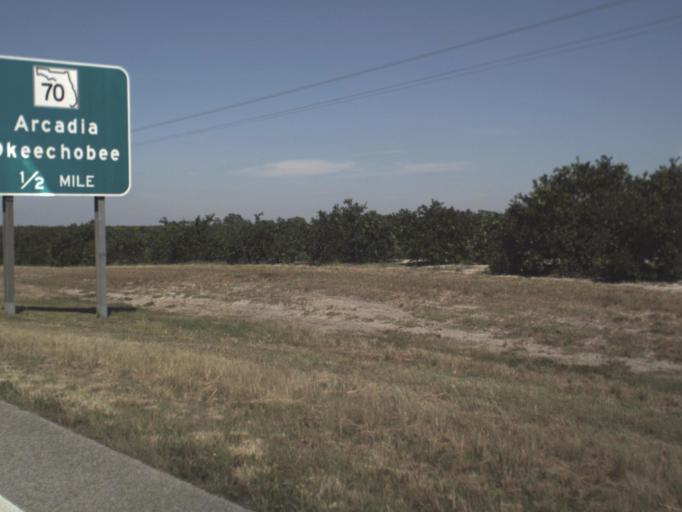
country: US
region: Florida
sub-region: Highlands County
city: Placid Lakes
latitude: 27.2001
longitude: -81.3285
